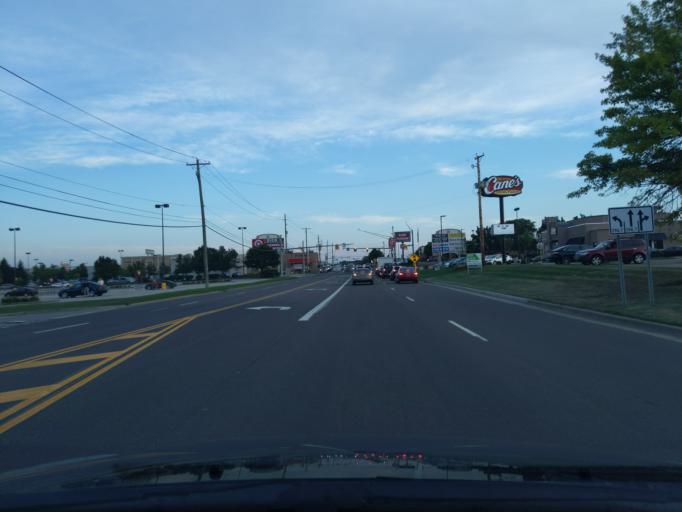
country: US
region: Ohio
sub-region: Stark County
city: North Canton
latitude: 40.8617
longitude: -81.4325
